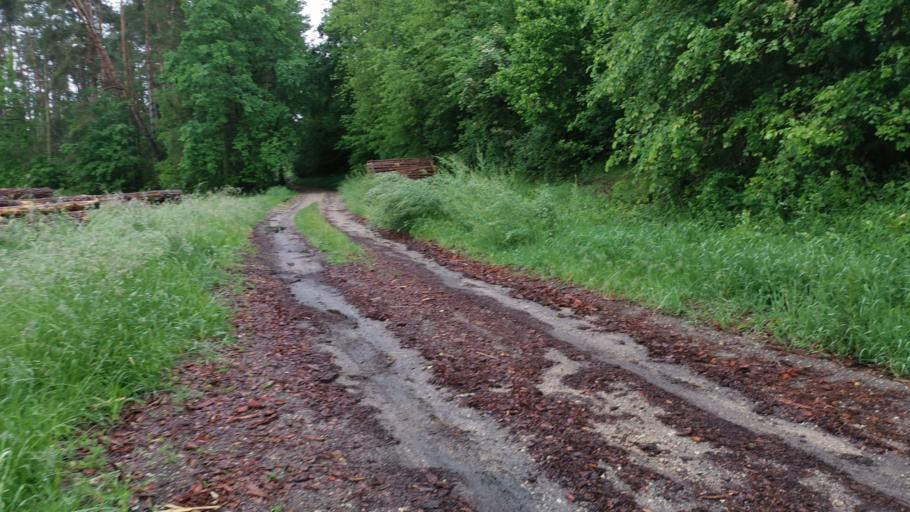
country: DE
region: Bavaria
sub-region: Regierungsbezirk Mittelfranken
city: Roth
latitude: 49.2571
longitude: 11.1099
